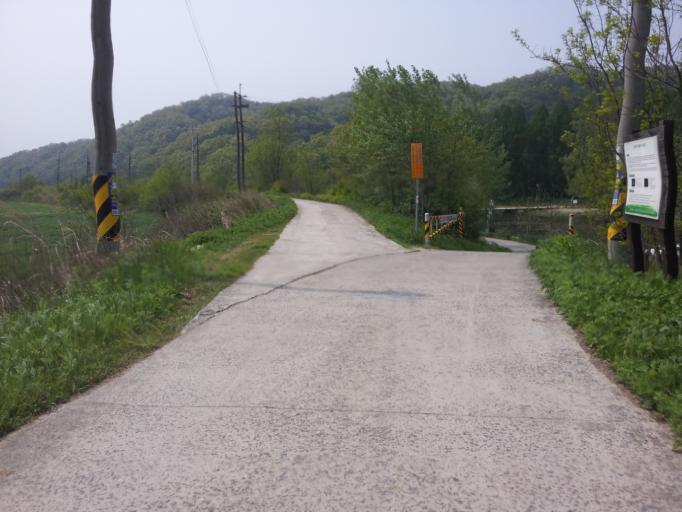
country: KR
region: Daejeon
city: Daejeon
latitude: 36.2784
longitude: 127.3343
